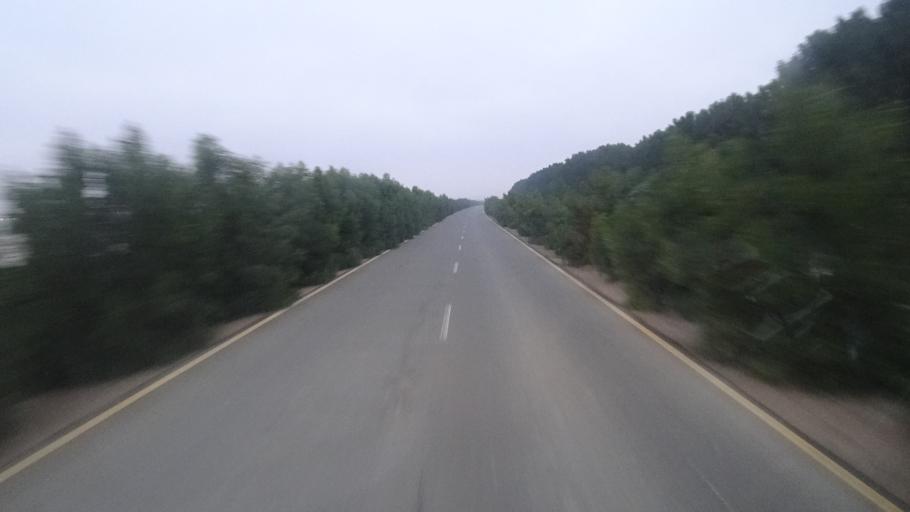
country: AE
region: Abu Dhabi
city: Abu Dhabi
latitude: 24.1859
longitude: 54.6971
